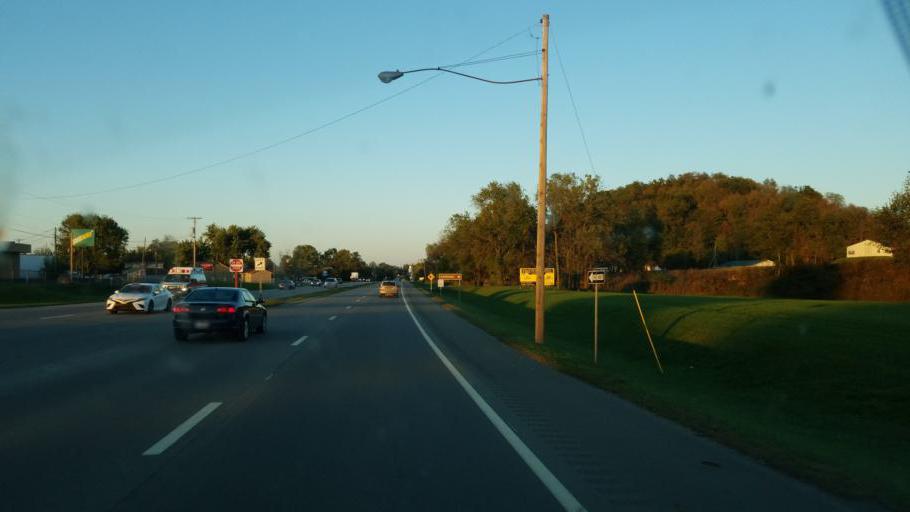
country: US
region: Ohio
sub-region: Pike County
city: Piketon
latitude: 39.0622
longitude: -83.0167
